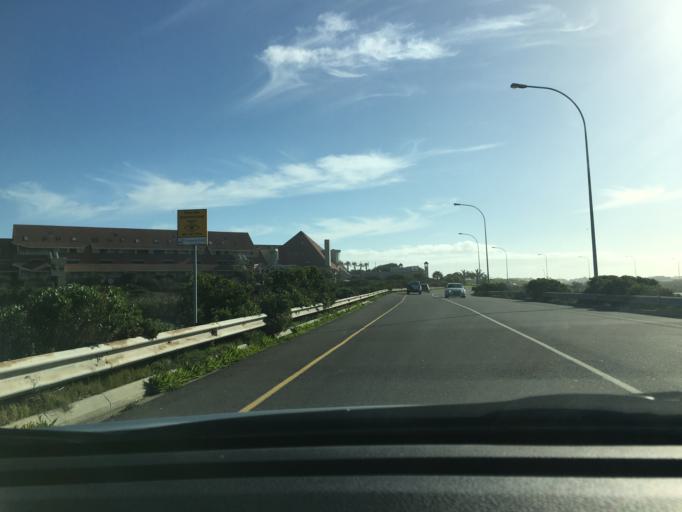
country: ZA
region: Western Cape
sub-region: City of Cape Town
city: Sunset Beach
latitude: -33.8299
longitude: 18.4837
